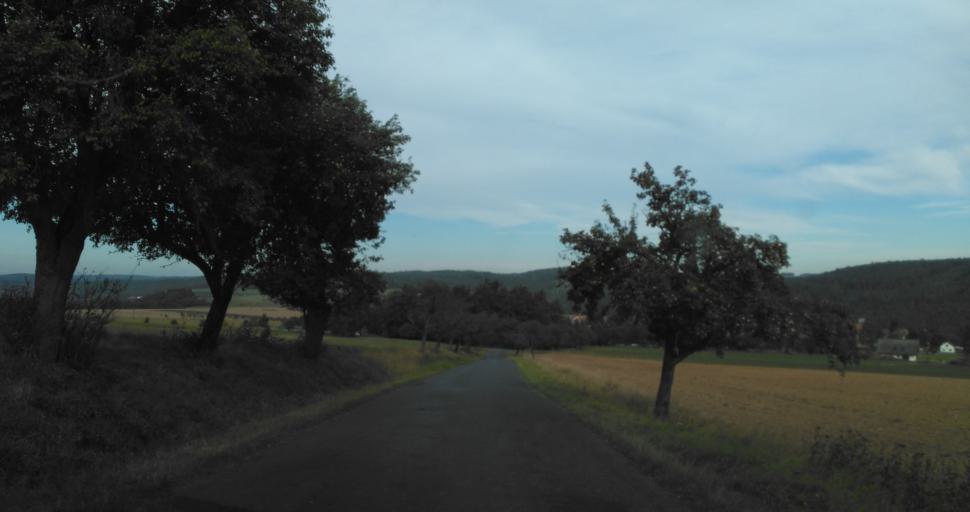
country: CZ
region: Plzensky
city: Zbiroh
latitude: 49.9592
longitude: 13.7717
